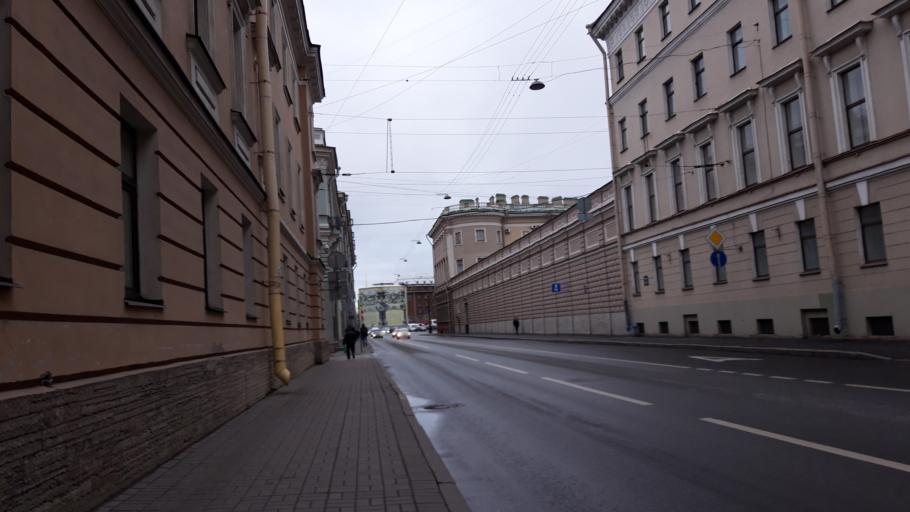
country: RU
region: St.-Petersburg
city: Saint Petersburg
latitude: 59.9294
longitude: 30.3083
